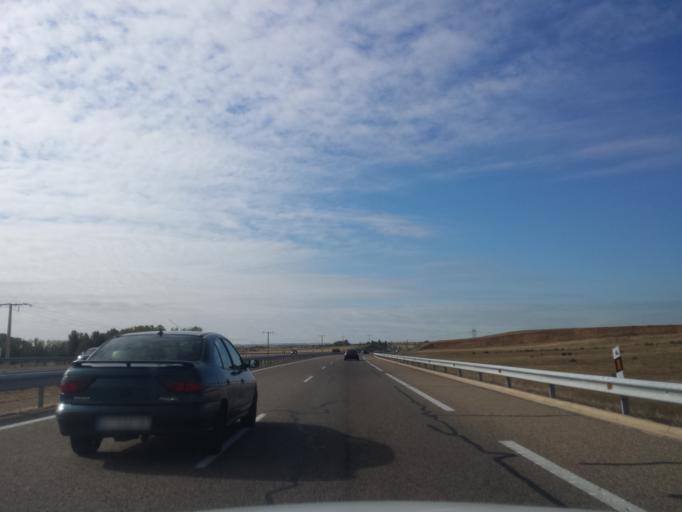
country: ES
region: Castille and Leon
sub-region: Provincia de Leon
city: Ardon
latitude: 42.4609
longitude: -5.5820
